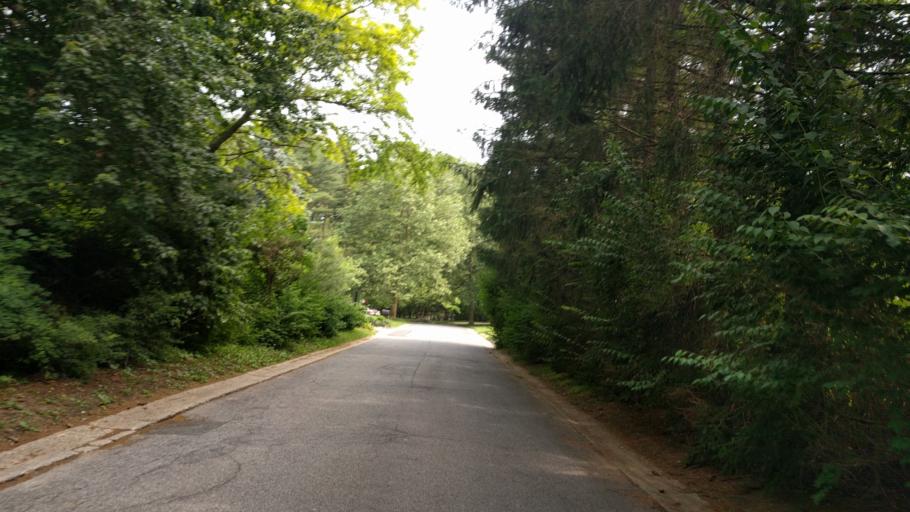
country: US
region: New York
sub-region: Nassau County
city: Old Brookville
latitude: 40.8473
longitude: -73.6072
